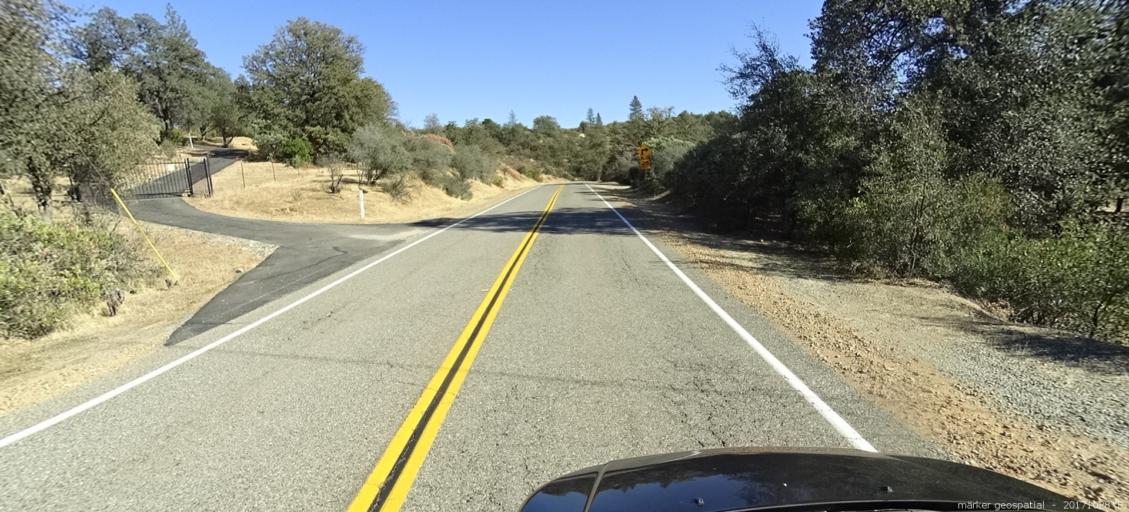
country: US
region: California
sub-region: Shasta County
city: Shasta
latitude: 40.6156
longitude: -122.4569
